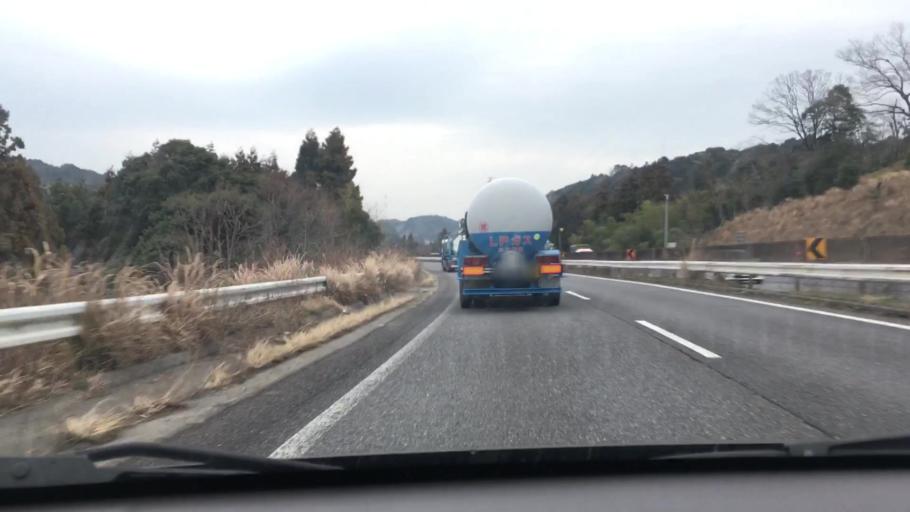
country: JP
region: Mie
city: Kameyama
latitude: 34.8381
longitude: 136.3854
